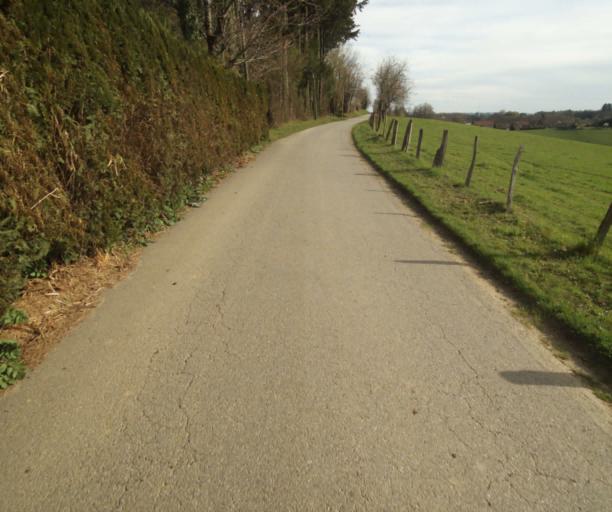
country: FR
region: Limousin
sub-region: Departement de la Correze
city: Naves
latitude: 45.3179
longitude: 1.7470
